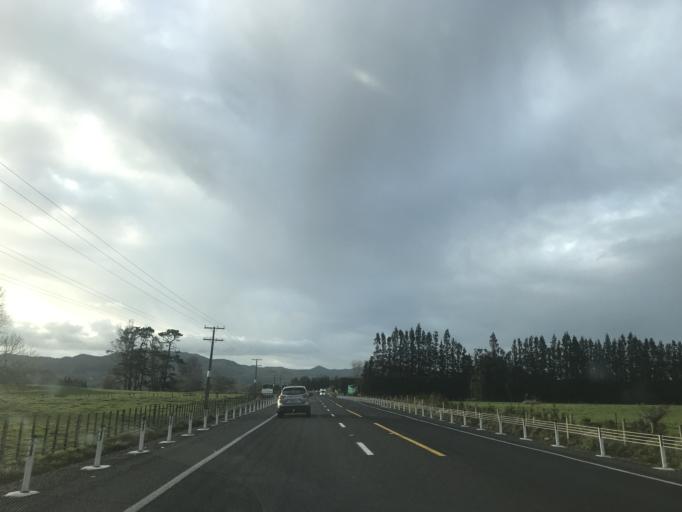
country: NZ
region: Waikato
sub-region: Hauraki District
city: Waihi
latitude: -37.4156
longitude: 175.8650
